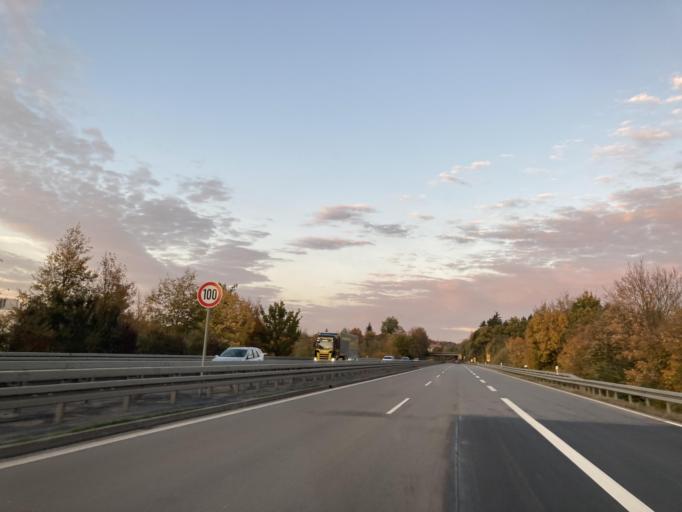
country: DE
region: Baden-Wuerttemberg
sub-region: Tuebingen Region
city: Balingen
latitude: 48.2662
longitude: 8.8531
